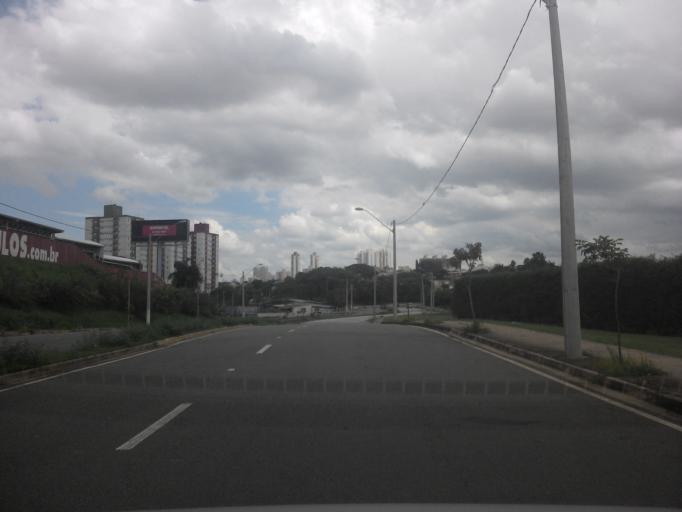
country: BR
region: Sao Paulo
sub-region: Campinas
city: Campinas
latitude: -22.8737
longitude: -47.0347
